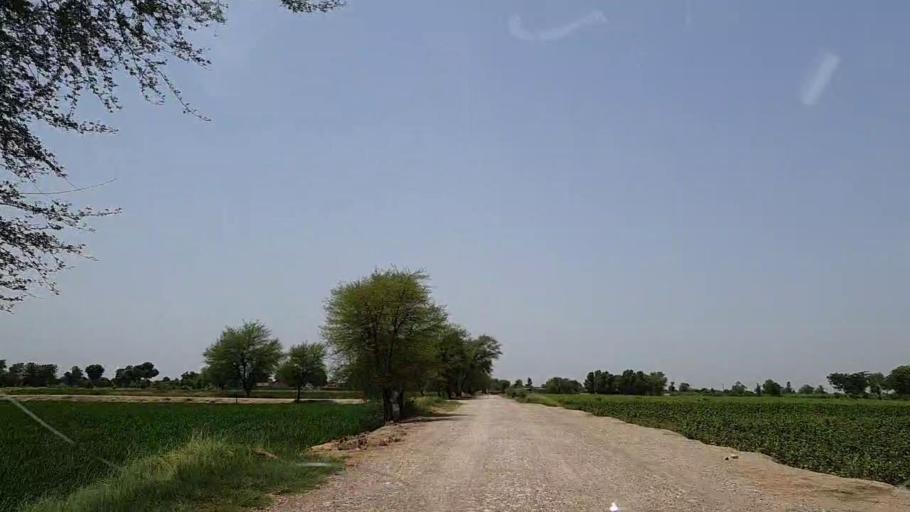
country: PK
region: Sindh
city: Tharu Shah
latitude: 26.9374
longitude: 68.0451
